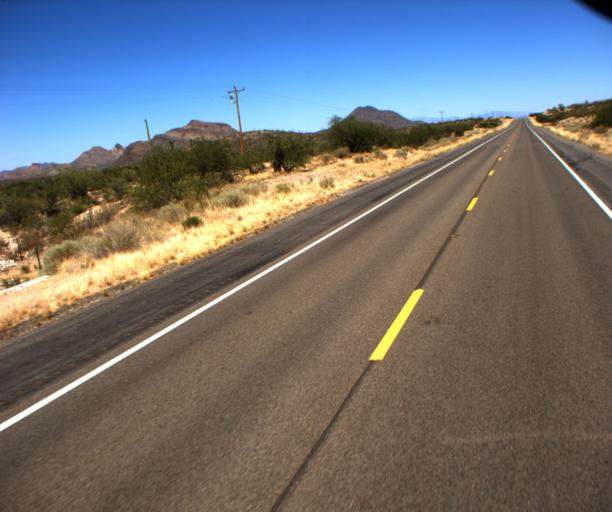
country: US
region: Arizona
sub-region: Pima County
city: Three Points
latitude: 32.0367
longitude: -111.5296
